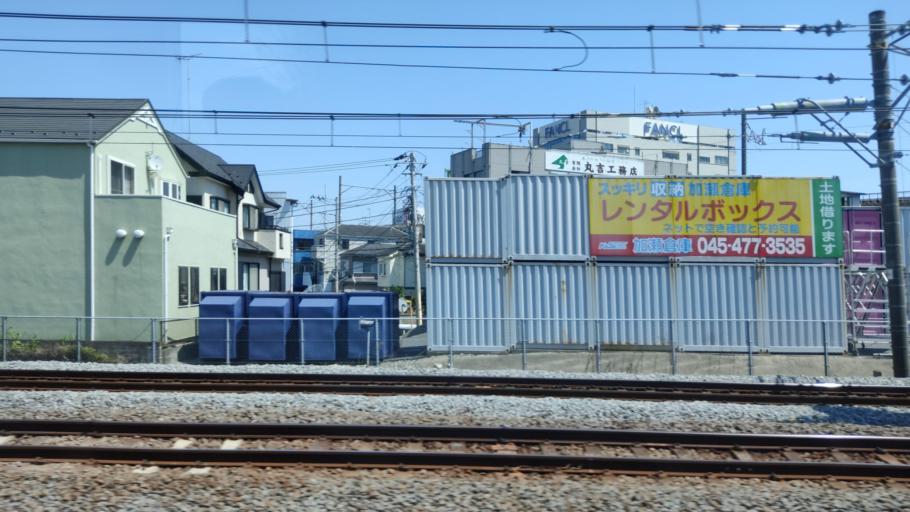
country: JP
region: Kanagawa
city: Kamakura
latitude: 35.3666
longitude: 139.5305
